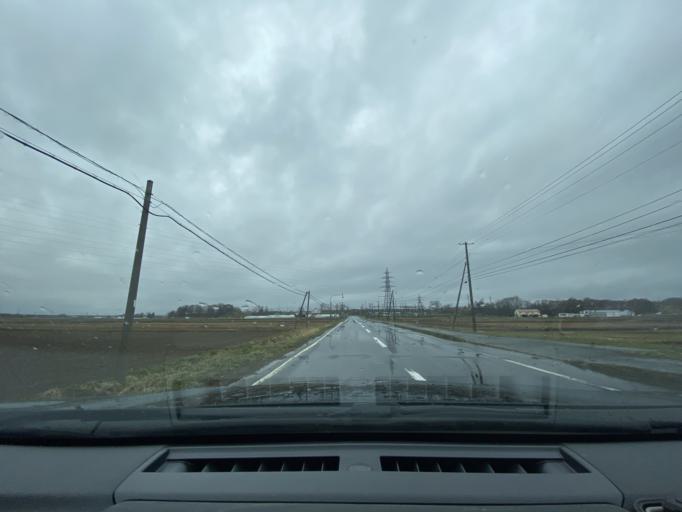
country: JP
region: Hokkaido
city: Fukagawa
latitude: 43.8127
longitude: 141.9555
